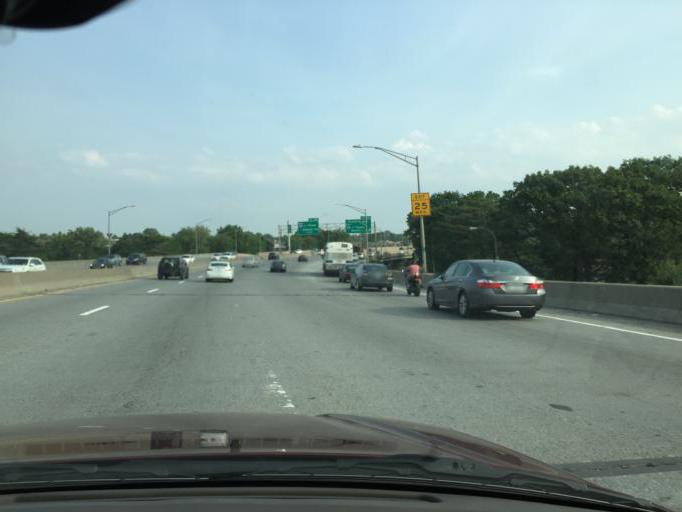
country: US
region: New York
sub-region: Queens County
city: Jamaica
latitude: 40.7503
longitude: -73.8353
